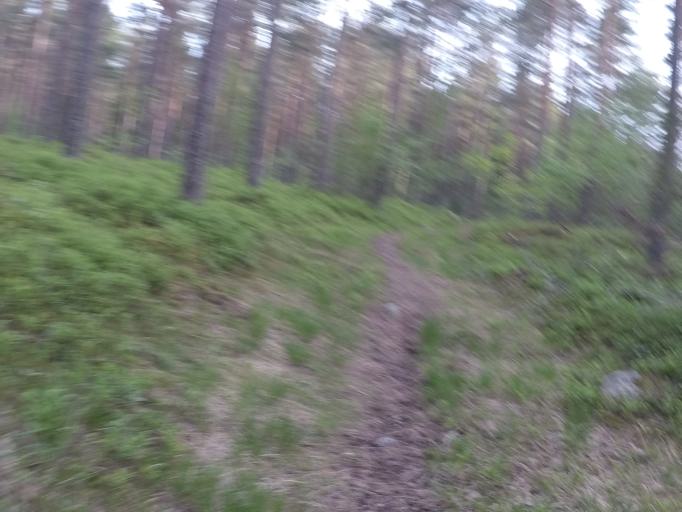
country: SE
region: Soedermanland
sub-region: Eskilstuna Kommun
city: Kvicksund
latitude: 59.4123
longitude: 16.3142
